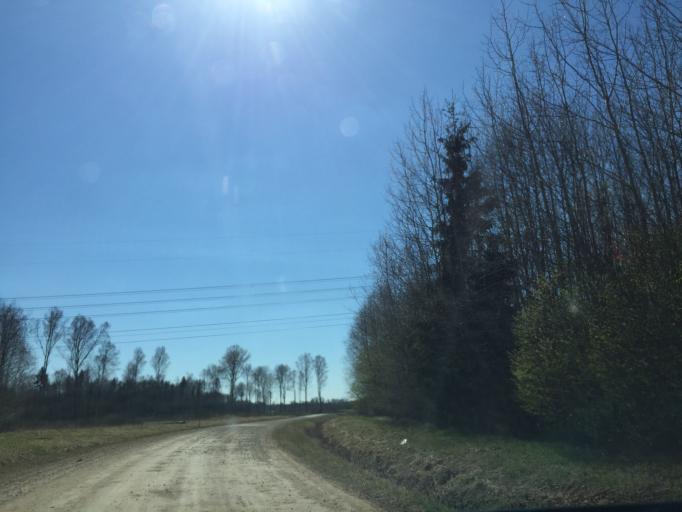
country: EE
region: Viljandimaa
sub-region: Viiratsi vald
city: Viiratsi
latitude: 58.4063
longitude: 25.8720
